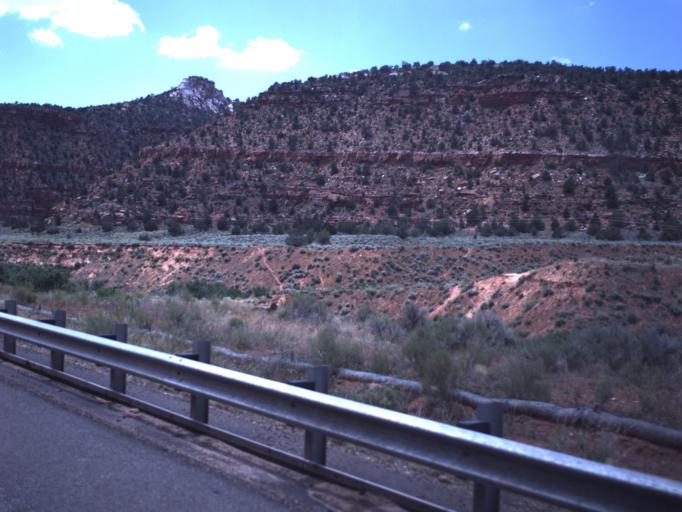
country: US
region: Utah
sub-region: Kane County
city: Kanab
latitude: 37.0728
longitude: -112.5364
